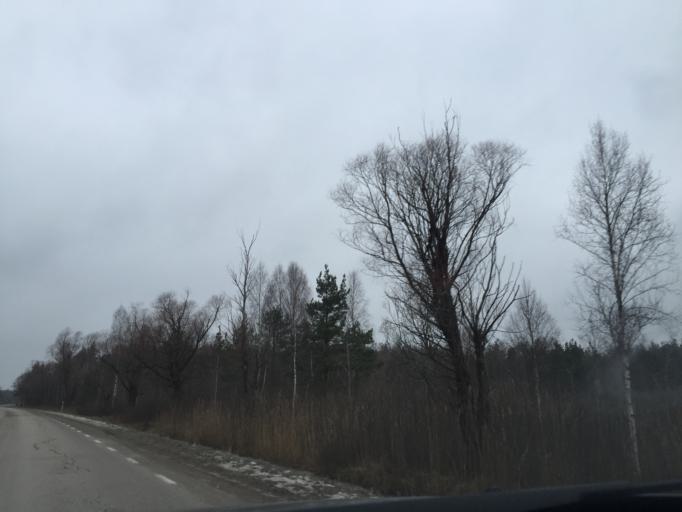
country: EE
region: Saare
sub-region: Kuressaare linn
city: Kuressaare
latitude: 58.2748
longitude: 22.4507
